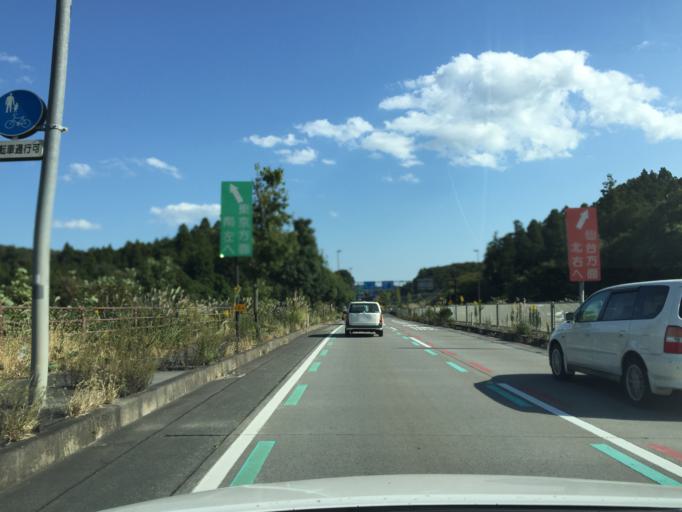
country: JP
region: Fukushima
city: Iwaki
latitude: 37.0216
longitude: 140.8904
